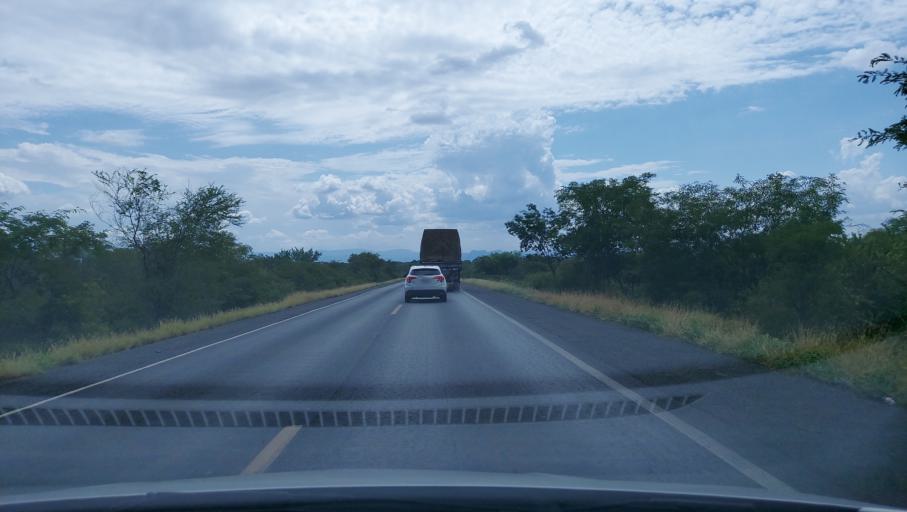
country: BR
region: Bahia
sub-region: Oliveira Dos Brejinhos
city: Beira Rio
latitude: -12.3237
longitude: -42.5702
